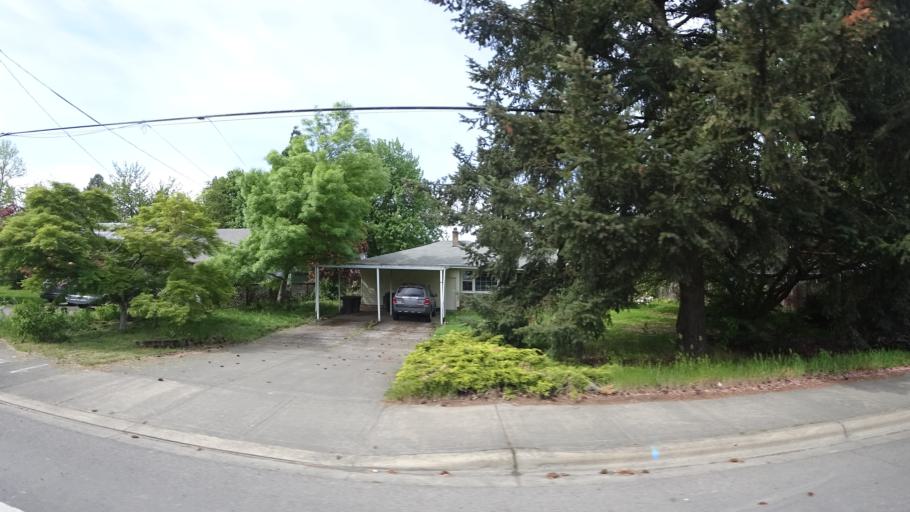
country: US
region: Oregon
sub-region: Washington County
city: Hillsboro
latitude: 45.5200
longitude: -122.9471
